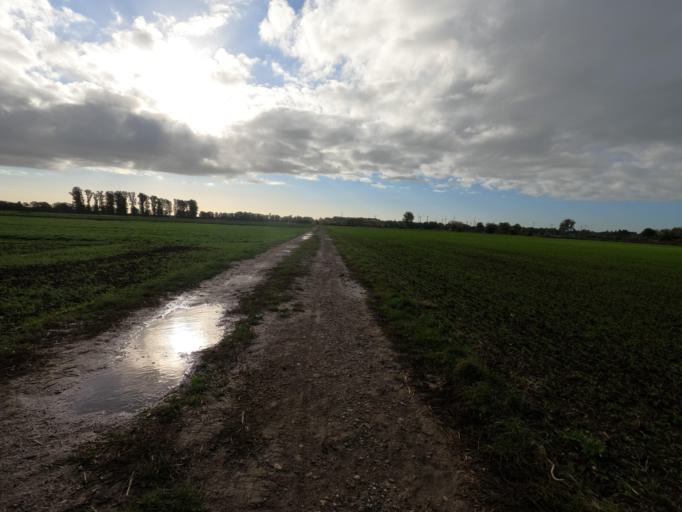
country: DE
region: North Rhine-Westphalia
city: Huckelhoven
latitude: 51.0216
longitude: 6.2339
